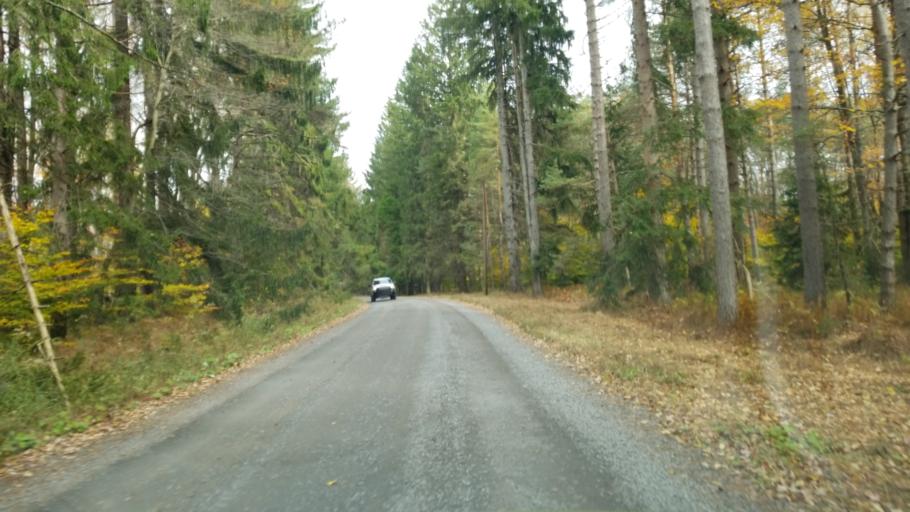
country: US
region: Pennsylvania
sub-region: Clearfield County
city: Clearfield
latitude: 41.1999
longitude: -78.4304
